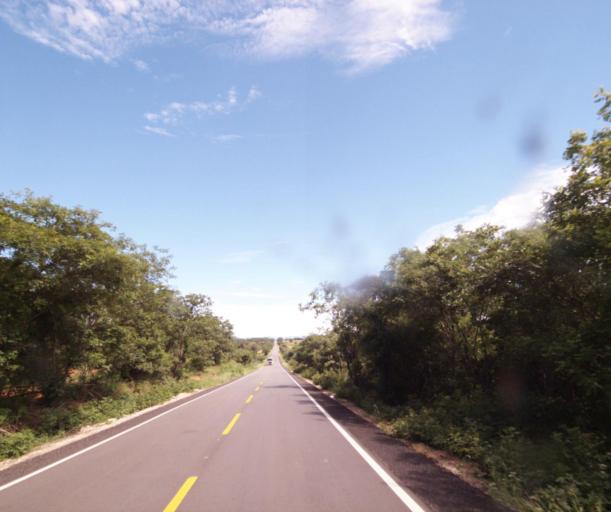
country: BR
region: Bahia
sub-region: Guanambi
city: Guanambi
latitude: -14.3939
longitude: -42.7561
